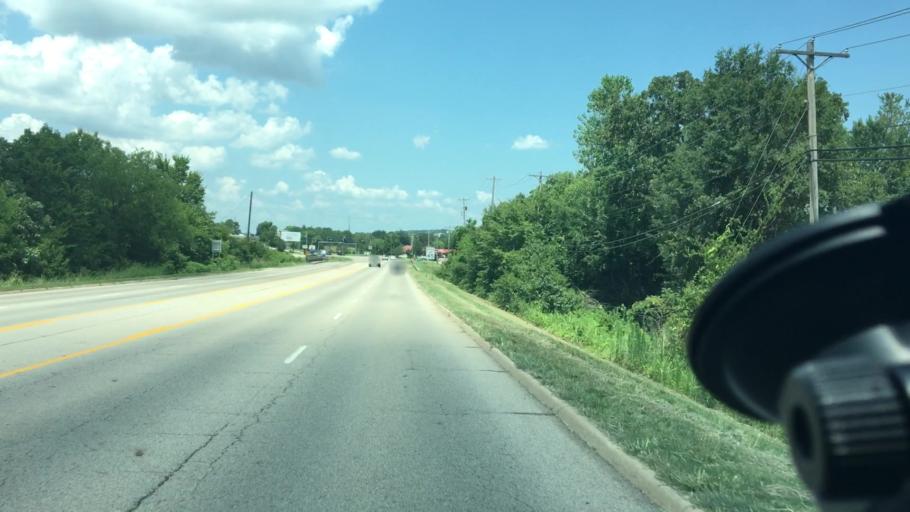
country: US
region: Arkansas
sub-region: Sebastian County
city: Barling
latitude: 35.3418
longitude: -94.3227
